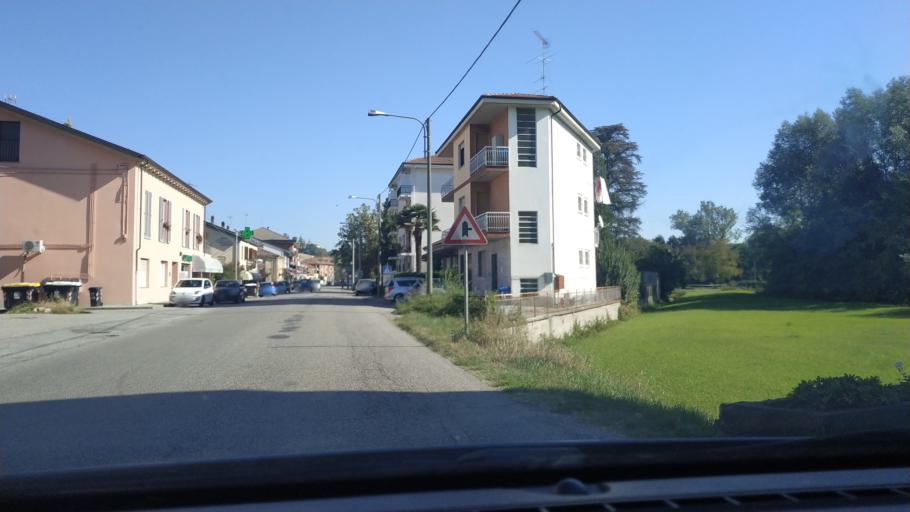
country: IT
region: Piedmont
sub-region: Provincia di Alessandria
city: Cerrina
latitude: 45.1126
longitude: 8.2105
